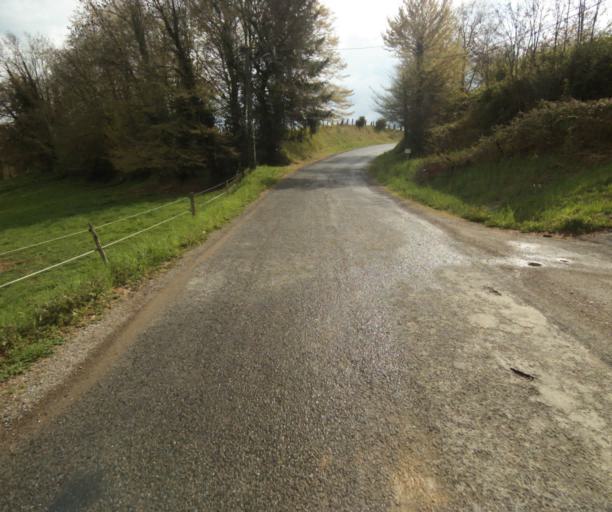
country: FR
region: Limousin
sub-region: Departement de la Correze
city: Tulle
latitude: 45.2834
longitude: 1.7519
